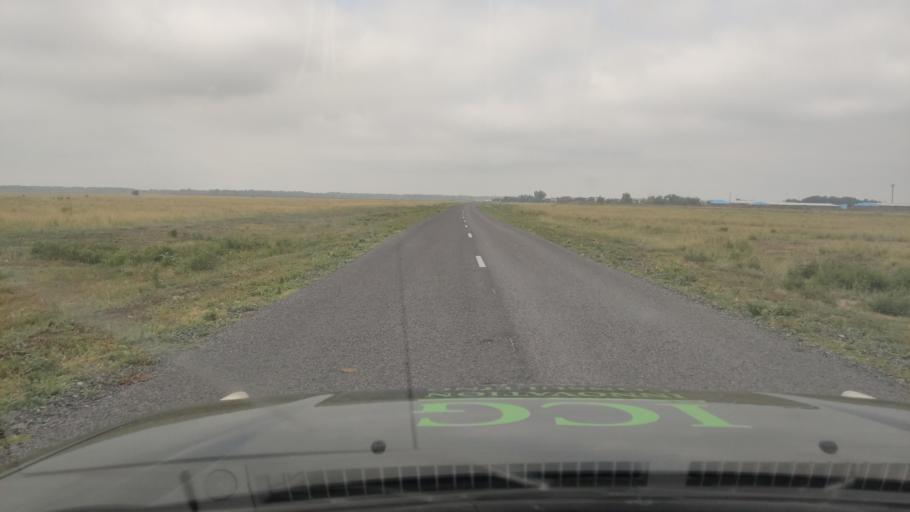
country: KZ
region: Pavlodar
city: Aksu
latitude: 51.9390
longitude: 77.3122
